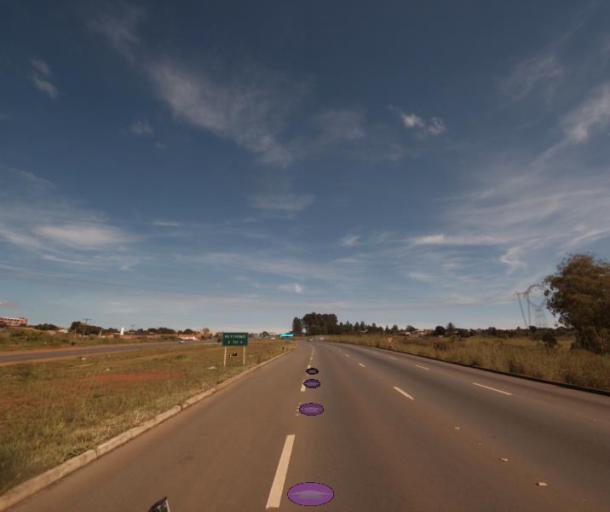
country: BR
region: Federal District
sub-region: Brasilia
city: Brasilia
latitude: -15.7614
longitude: -48.2384
